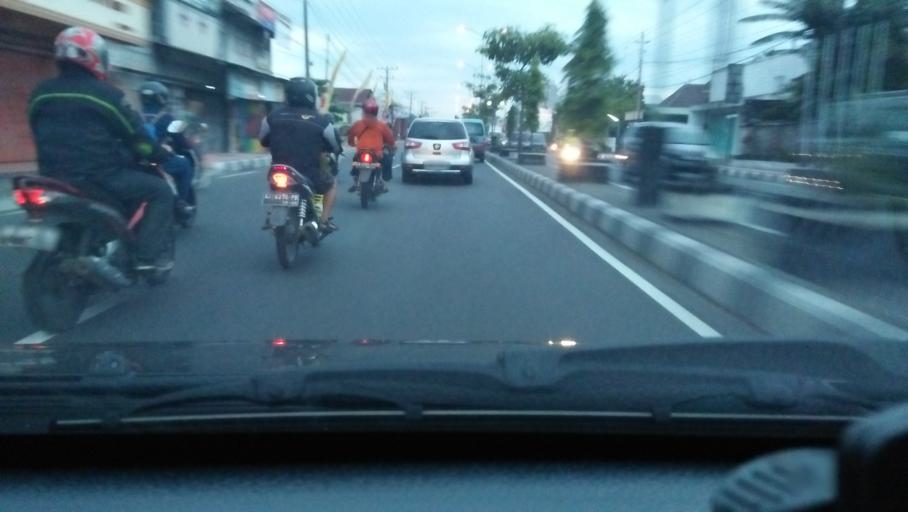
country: ID
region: Central Java
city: Mertoyudan
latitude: -7.5136
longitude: 110.2256
